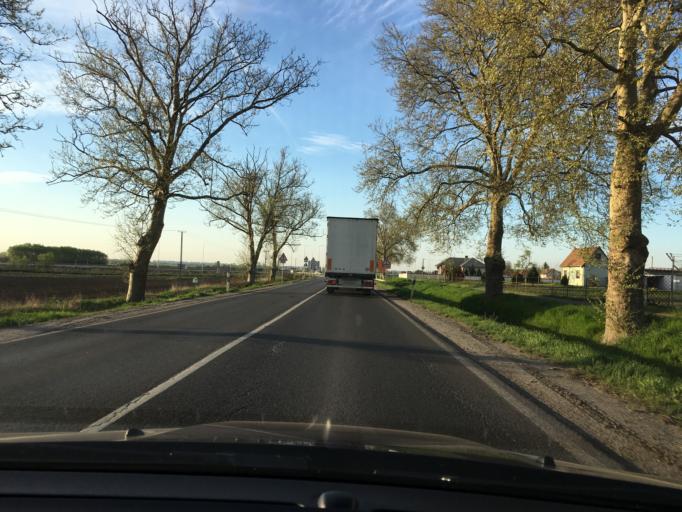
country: HU
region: Hajdu-Bihar
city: Mikepercs
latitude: 47.4601
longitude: 21.6366
